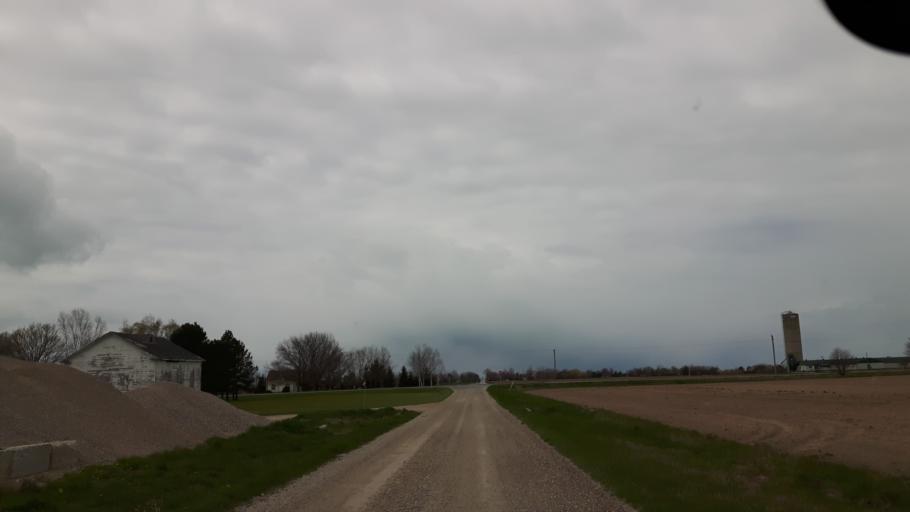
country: CA
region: Ontario
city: Bluewater
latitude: 43.4730
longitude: -81.6968
